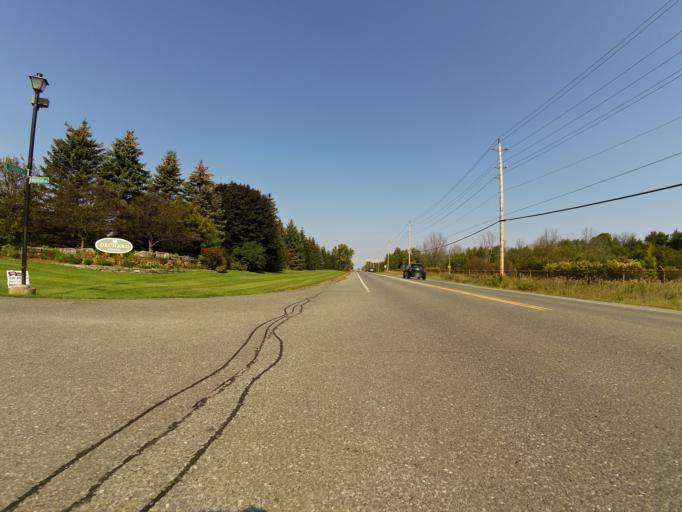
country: CA
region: Ontario
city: Bells Corners
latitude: 45.2830
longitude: -75.7826
